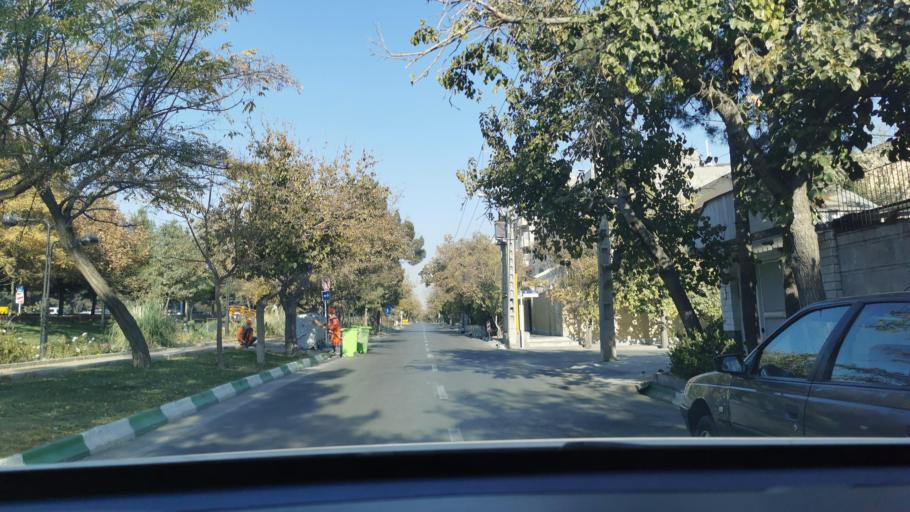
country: IR
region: Razavi Khorasan
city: Mashhad
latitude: 36.2908
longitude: 59.5518
